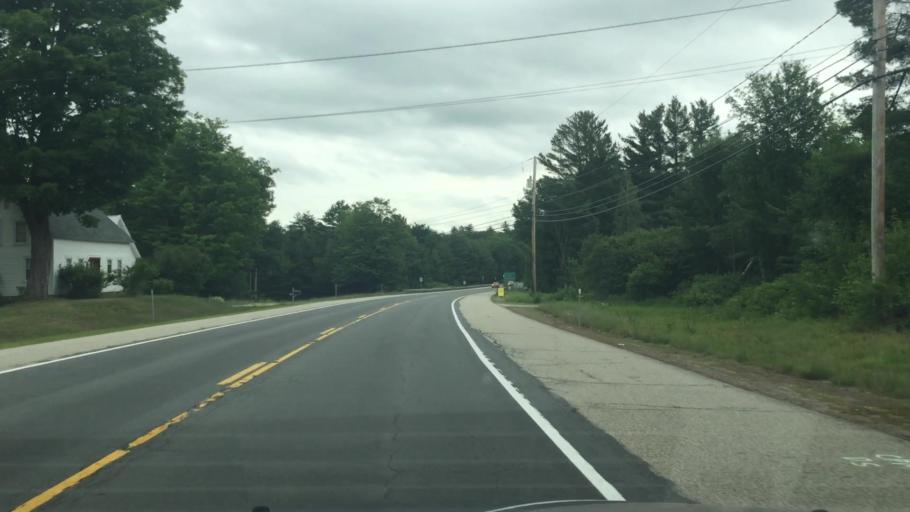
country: US
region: New Hampshire
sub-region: Carroll County
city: Tamworth
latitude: 43.8305
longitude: -71.2772
